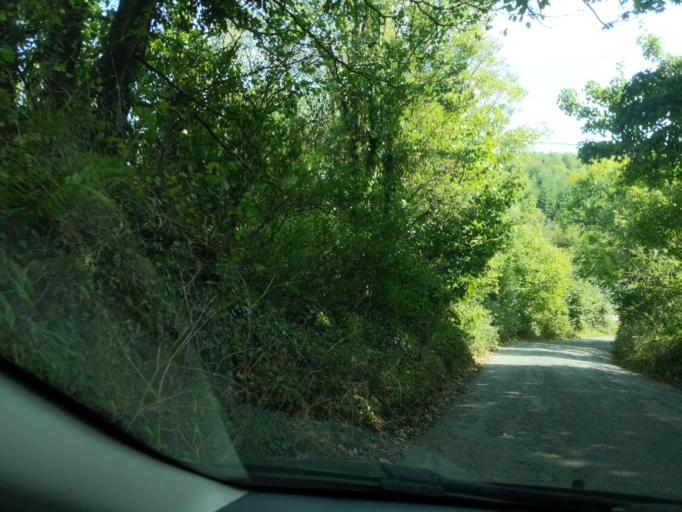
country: GB
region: England
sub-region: Cornwall
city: Torpoint
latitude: 50.3580
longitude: -4.2275
